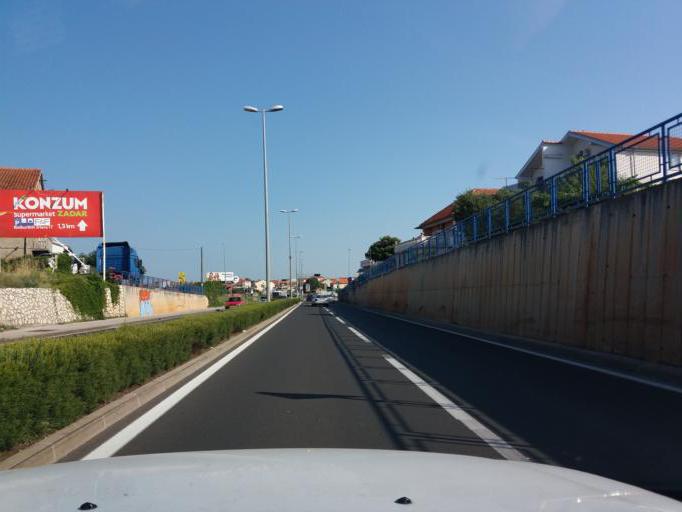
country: HR
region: Zadarska
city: Zadar
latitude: 44.1068
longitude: 15.2616
